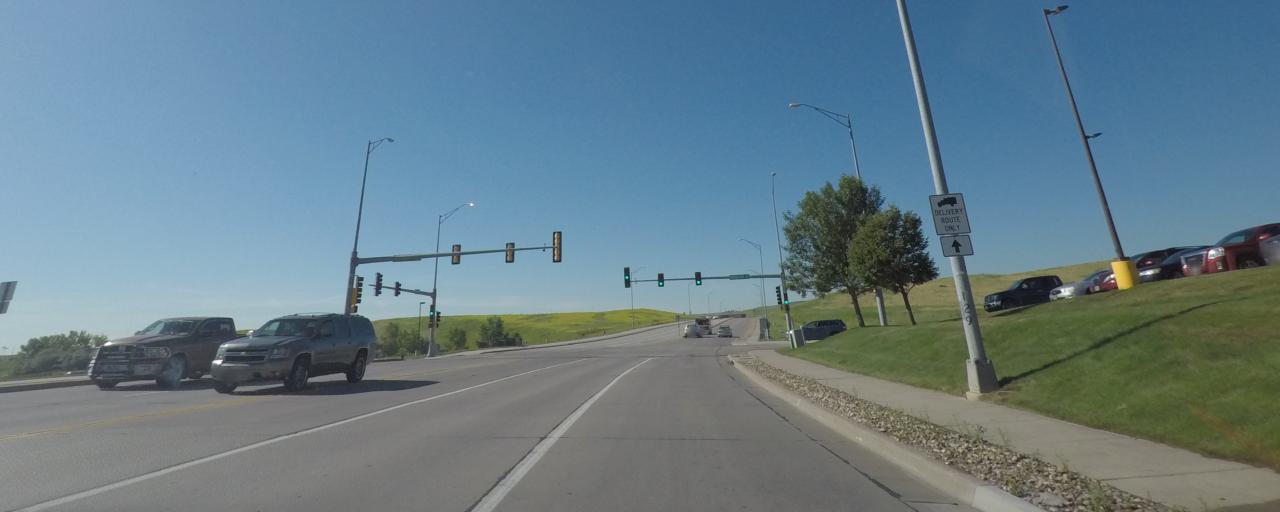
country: US
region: South Dakota
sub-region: Pennington County
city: Rapid City
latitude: 44.0434
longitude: -103.2192
